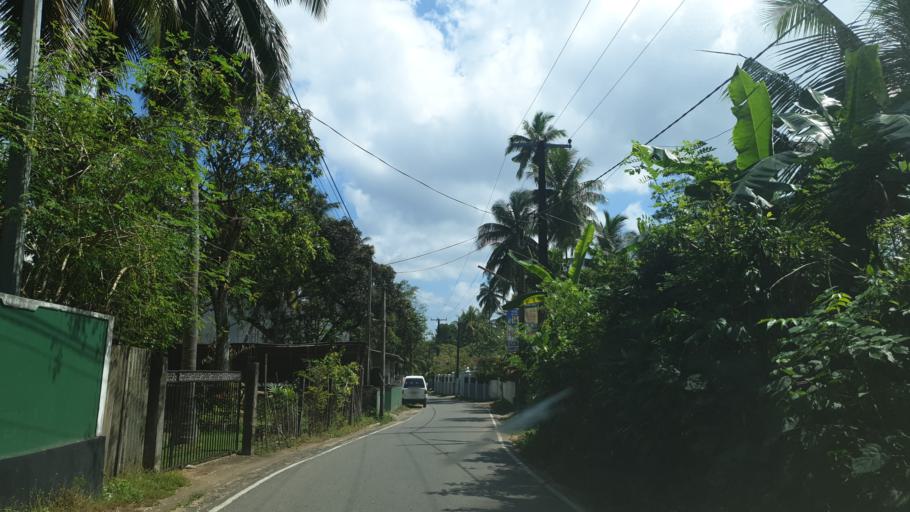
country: LK
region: Western
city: Panadura
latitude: 6.6740
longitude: 79.9355
